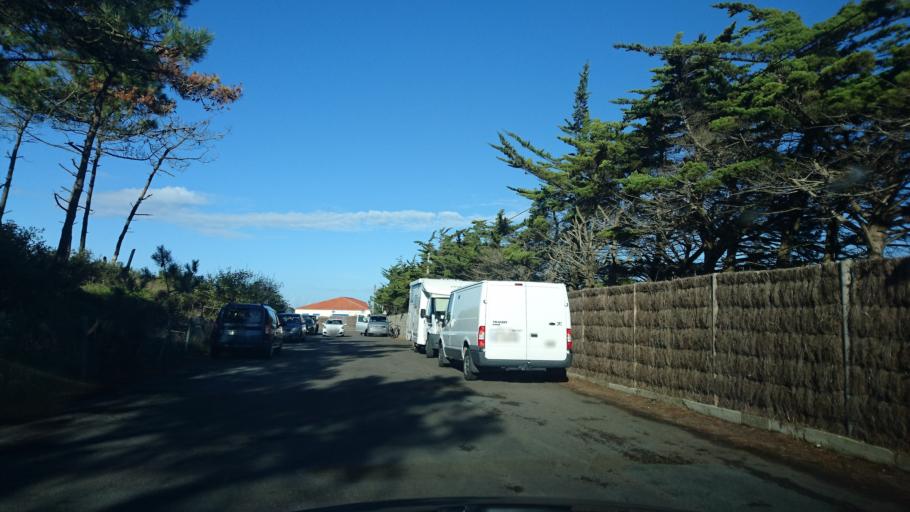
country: FR
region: Pays de la Loire
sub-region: Departement de la Vendee
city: Les Sables-d'Olonne
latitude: 46.5116
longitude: -1.8131
